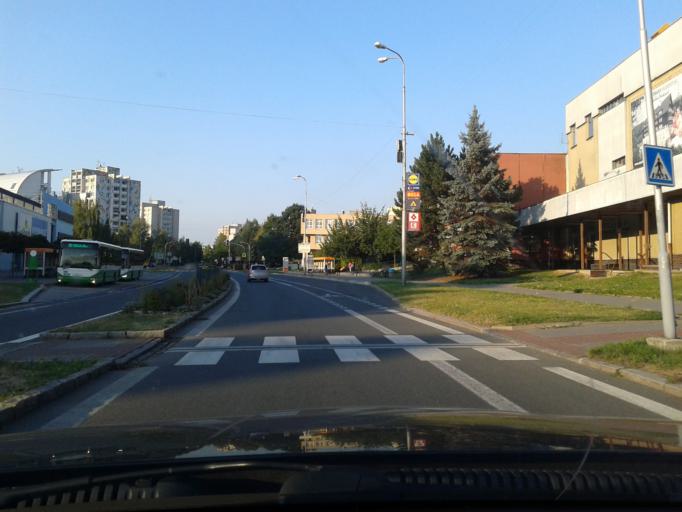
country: CZ
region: Moravskoslezsky
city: Orlova
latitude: 49.8706
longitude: 18.4251
